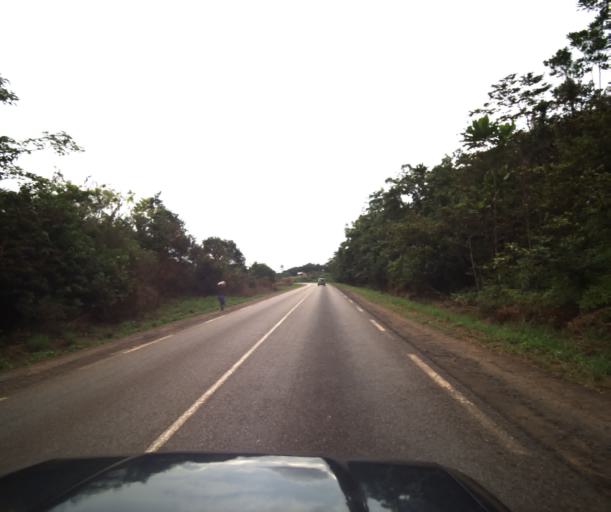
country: CM
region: Littoral
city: Edea
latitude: 3.8355
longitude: 10.4413
